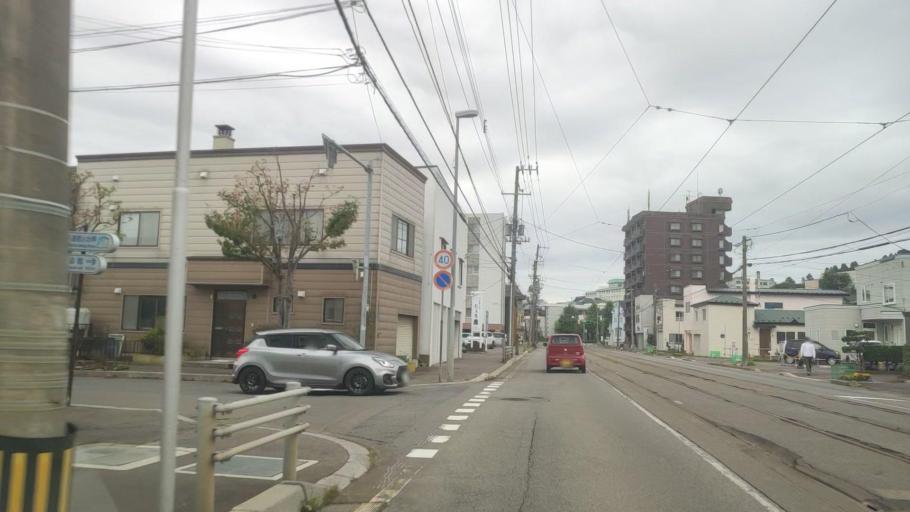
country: JP
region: Hokkaido
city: Hakodate
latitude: 41.7686
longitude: 140.7104
